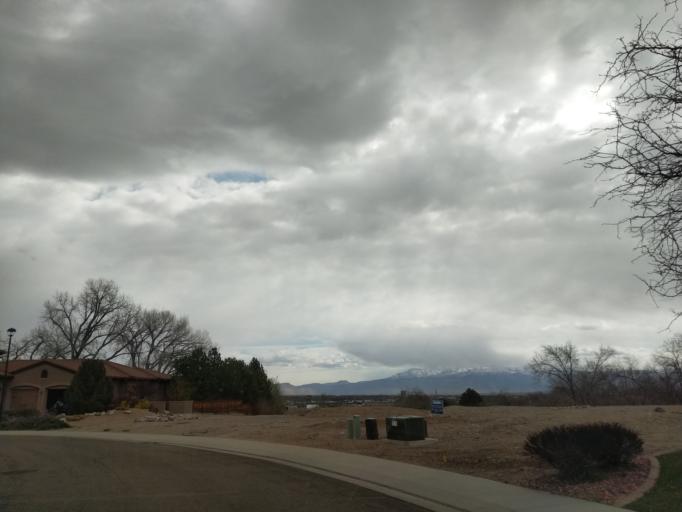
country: US
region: Colorado
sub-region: Mesa County
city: Redlands
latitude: 39.0663
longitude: -108.5961
